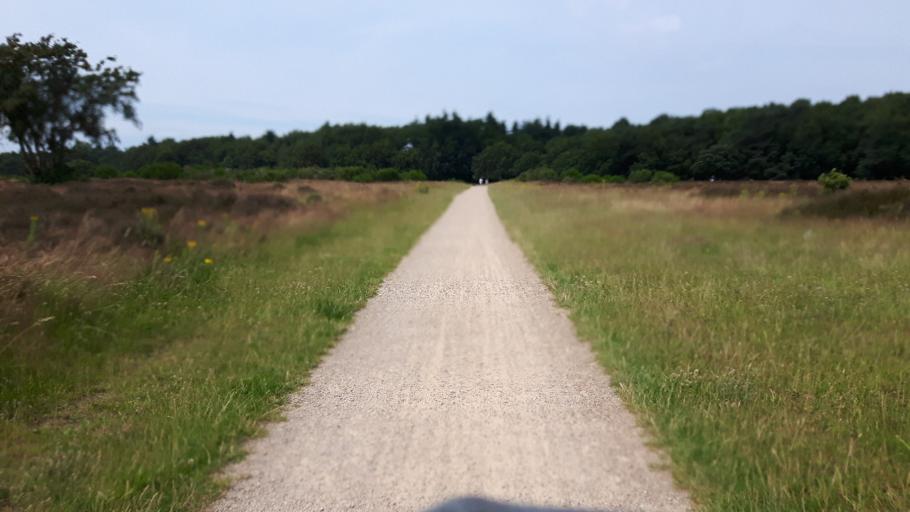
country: NL
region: North Holland
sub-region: Gemeente Hilversum
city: Hilversum
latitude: 52.2023
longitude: 5.1674
